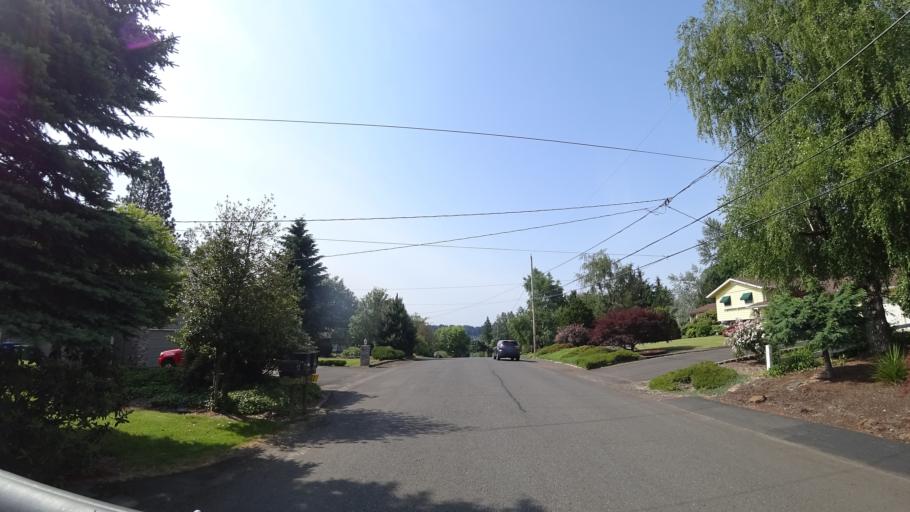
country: US
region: Oregon
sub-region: Clackamas County
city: Happy Valley
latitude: 45.4594
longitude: -122.5205
